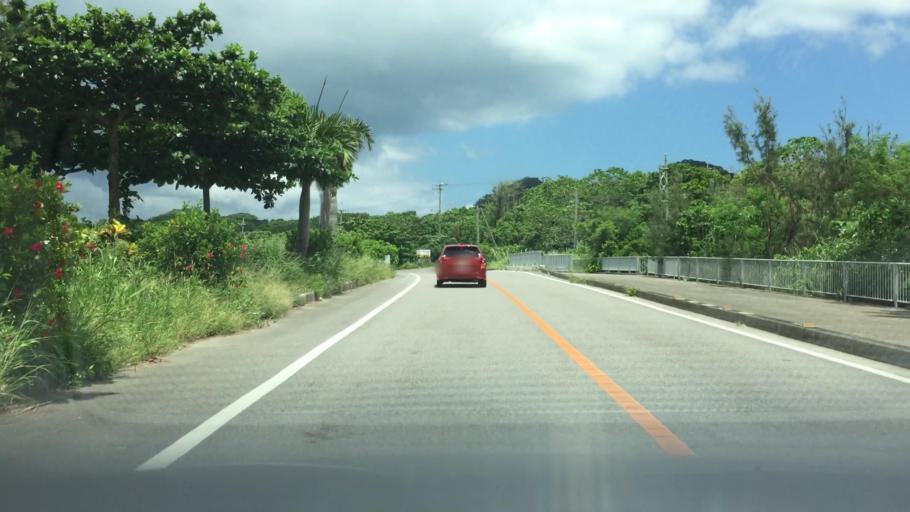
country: JP
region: Okinawa
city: Ishigaki
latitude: 24.4326
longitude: 124.1239
